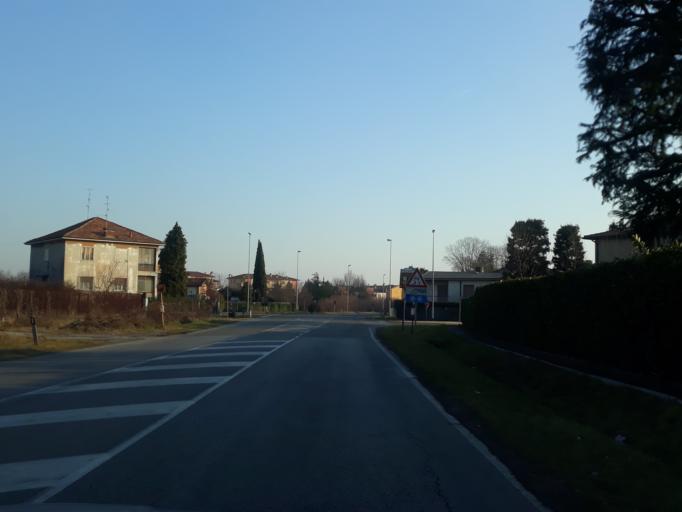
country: IT
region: Lombardy
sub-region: Provincia di Monza e Brianza
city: Bellusco
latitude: 45.6229
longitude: 9.4207
